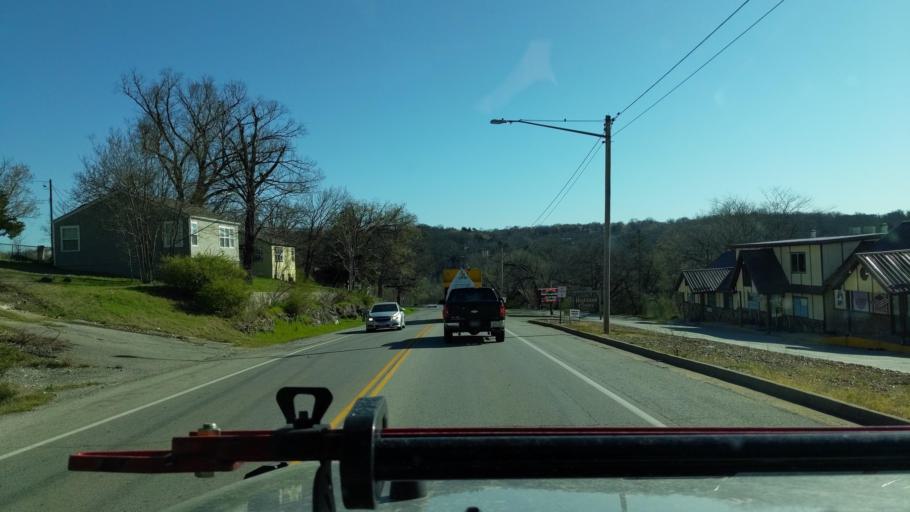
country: US
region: Missouri
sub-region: Taney County
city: Hollister
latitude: 36.6200
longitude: -93.2176
